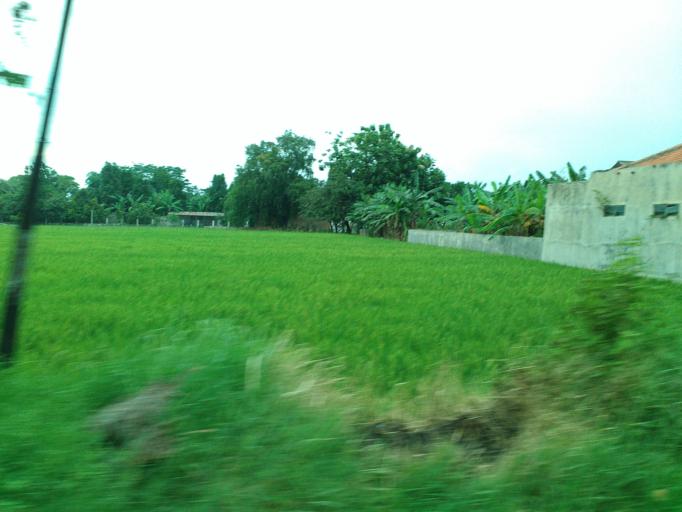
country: ID
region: Central Java
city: Delanggu
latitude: -7.6115
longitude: 110.7012
